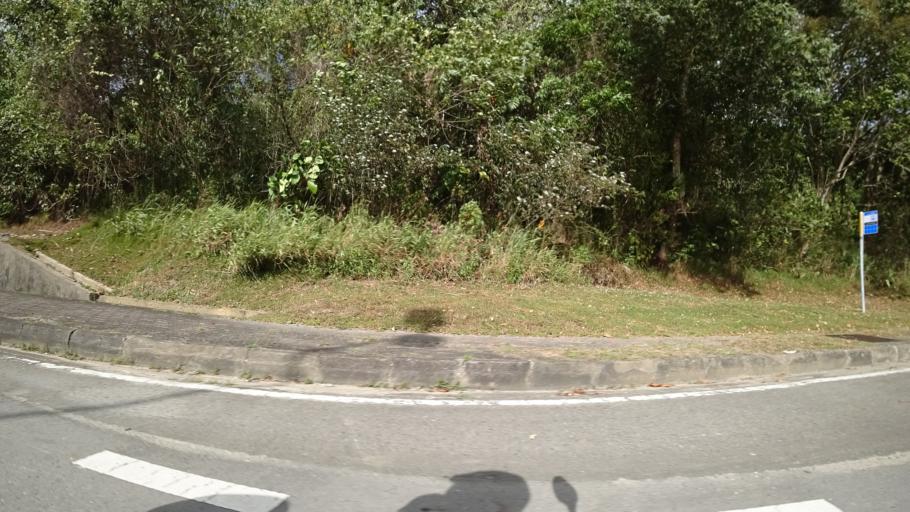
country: BN
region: Brunei and Muara
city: Bandar Seri Begawan
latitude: 4.8590
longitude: 114.8673
